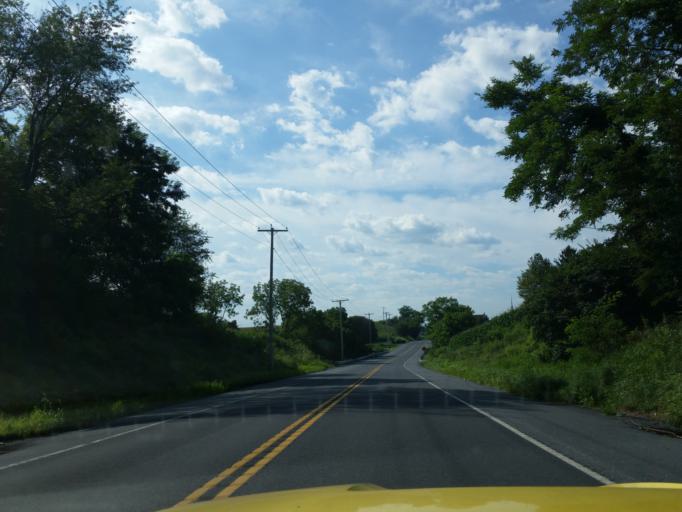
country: US
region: Pennsylvania
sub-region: Lebanon County
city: Fredericksburg
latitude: 40.4314
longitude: -76.4242
